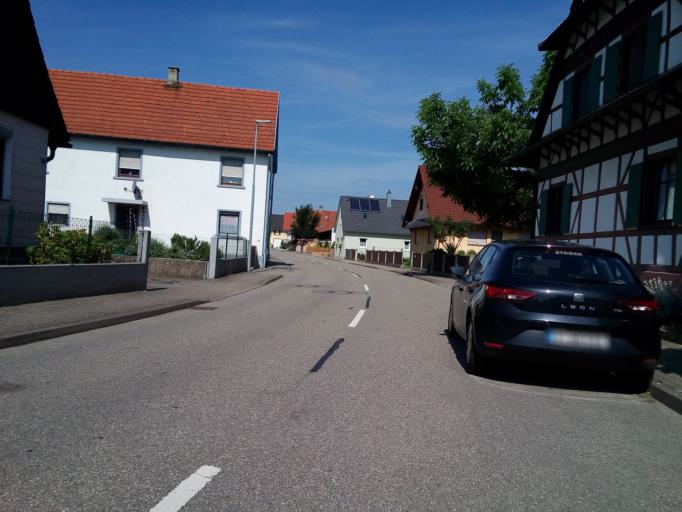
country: DE
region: Baden-Wuerttemberg
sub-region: Freiburg Region
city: Rheinau
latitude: 48.6228
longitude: 7.8968
